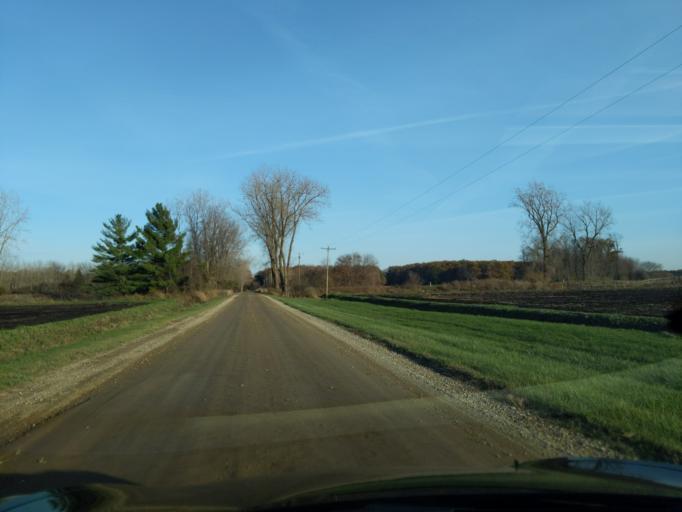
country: US
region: Michigan
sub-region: Clinton County
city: Bath
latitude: 42.7986
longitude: -84.4953
